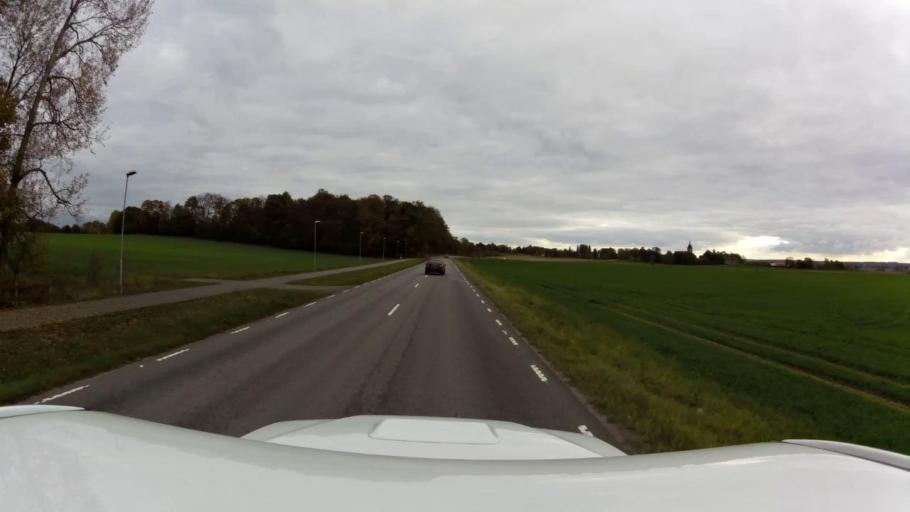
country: SE
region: OEstergoetland
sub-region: Linkopings Kommun
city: Berg
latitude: 58.4880
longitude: 15.5084
